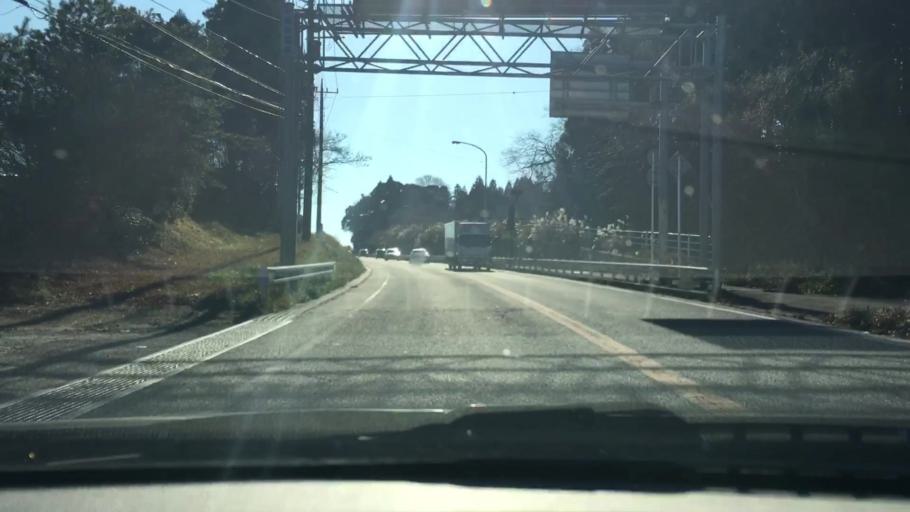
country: JP
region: Chiba
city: Sakura
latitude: 35.6935
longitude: 140.2456
